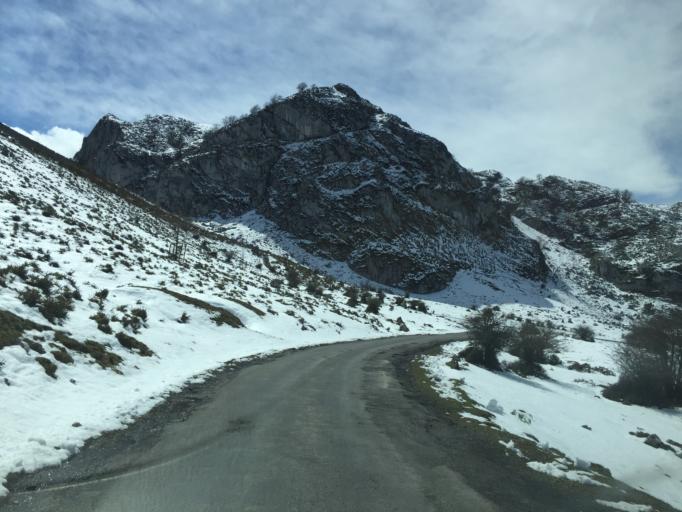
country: ES
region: Asturias
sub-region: Province of Asturias
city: Amieva
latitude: 43.2730
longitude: -4.9859
